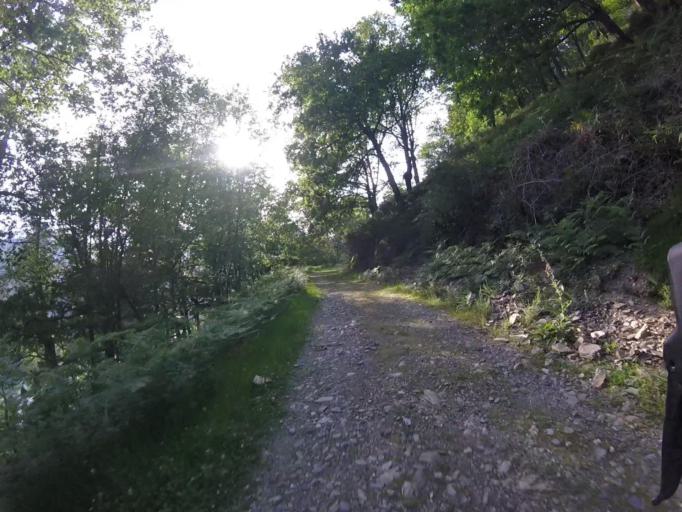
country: ES
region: Navarre
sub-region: Provincia de Navarra
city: Arano
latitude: 43.2316
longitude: -1.8740
